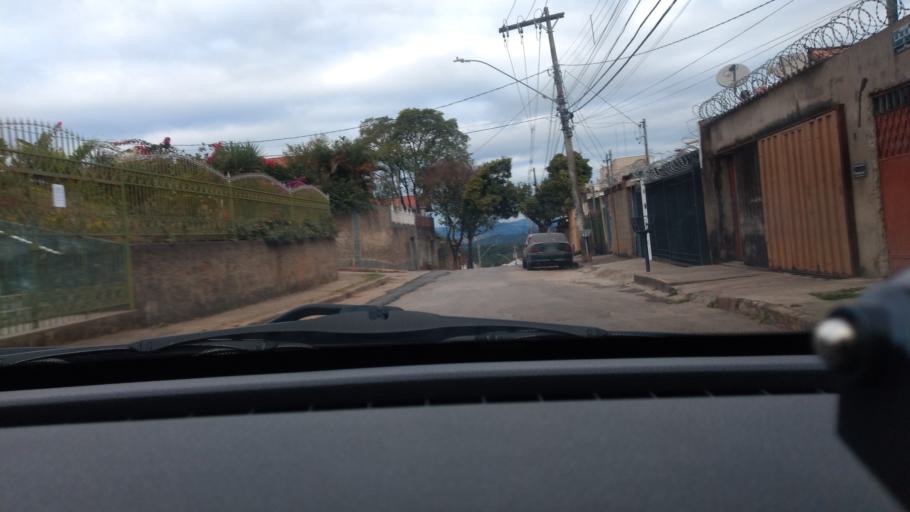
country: BR
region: Minas Gerais
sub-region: Santa Luzia
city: Santa Luzia
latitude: -19.8088
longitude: -43.9395
